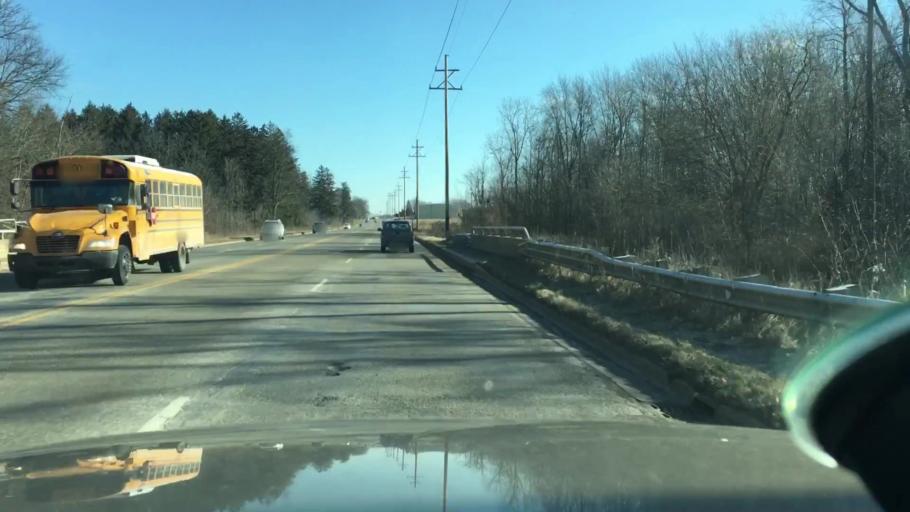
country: US
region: Michigan
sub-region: Jackson County
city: Jackson
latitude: 42.2910
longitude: -84.4060
